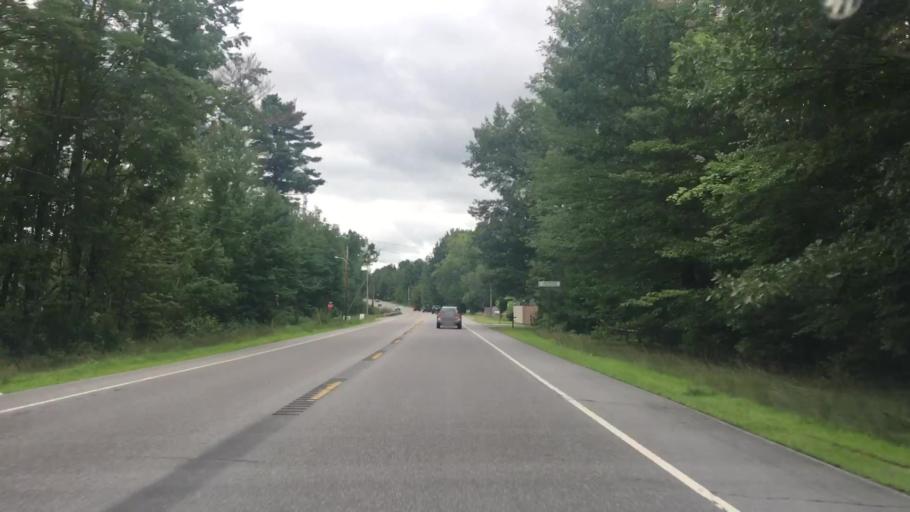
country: US
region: Maine
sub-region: York County
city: Alfred
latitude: 43.4944
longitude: -70.7194
